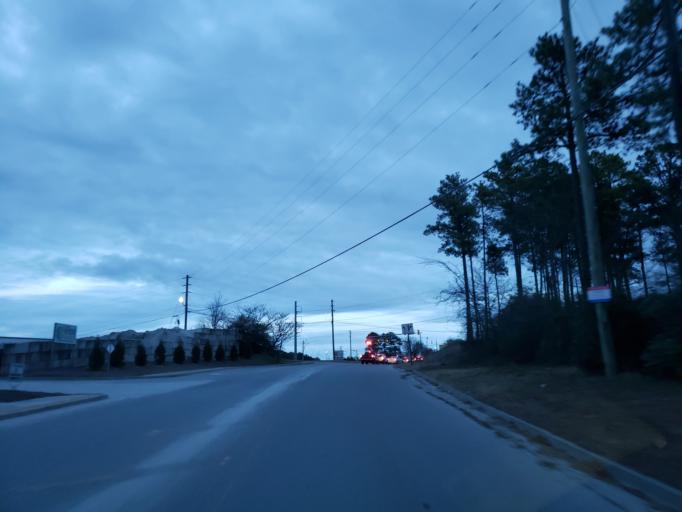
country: US
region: Georgia
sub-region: Cobb County
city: Kennesaw
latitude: 34.0215
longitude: -84.5929
